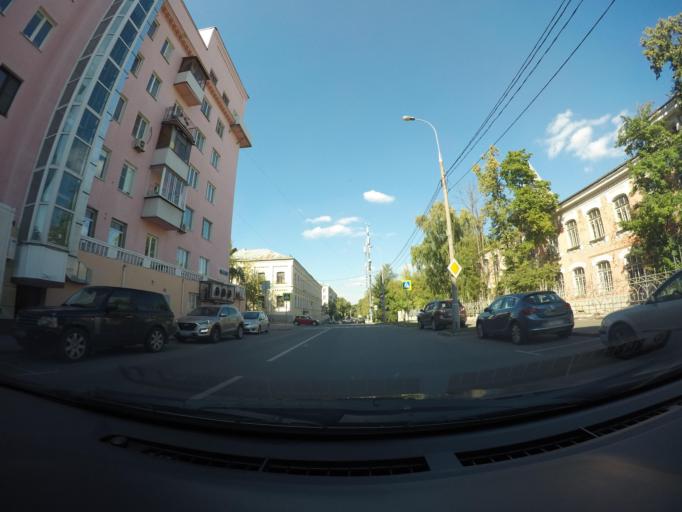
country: RU
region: Moscow
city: Sokol'niki
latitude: 55.7964
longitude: 37.6899
